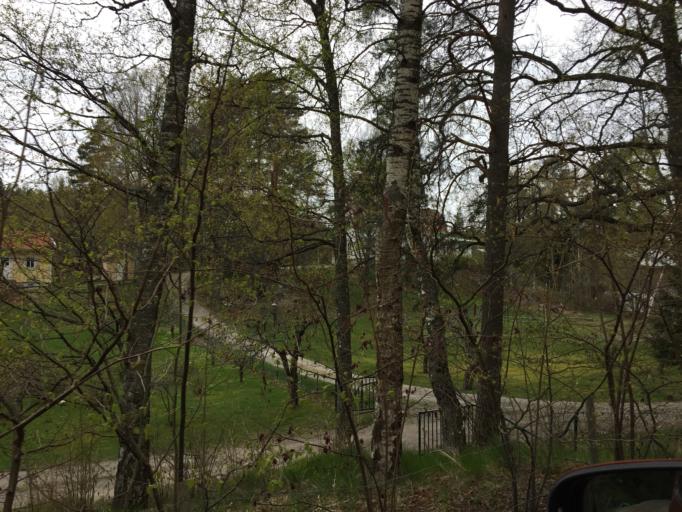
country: SE
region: Stockholm
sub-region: Salems Kommun
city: Ronninge
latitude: 59.1914
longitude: 17.7113
